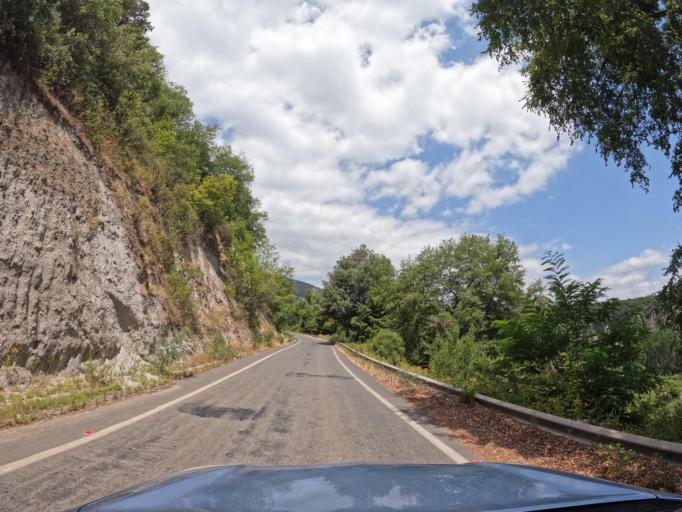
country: CL
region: Maule
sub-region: Provincia de Curico
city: Molina
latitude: -35.1813
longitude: -71.0794
